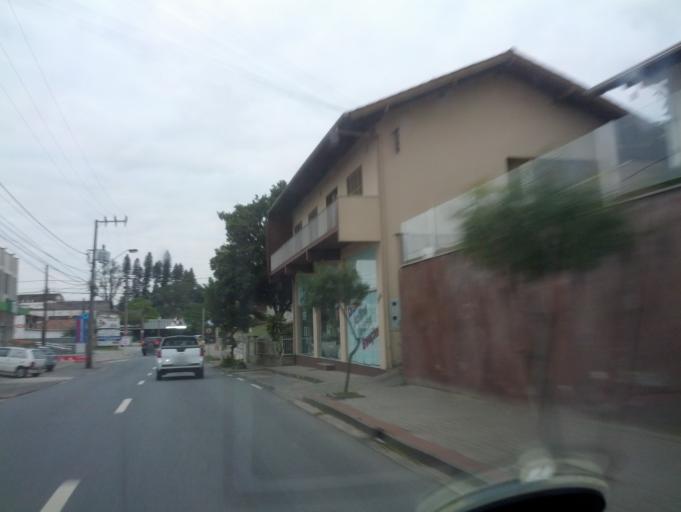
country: BR
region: Santa Catarina
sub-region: Blumenau
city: Blumenau
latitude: -26.8845
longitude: -49.0828
